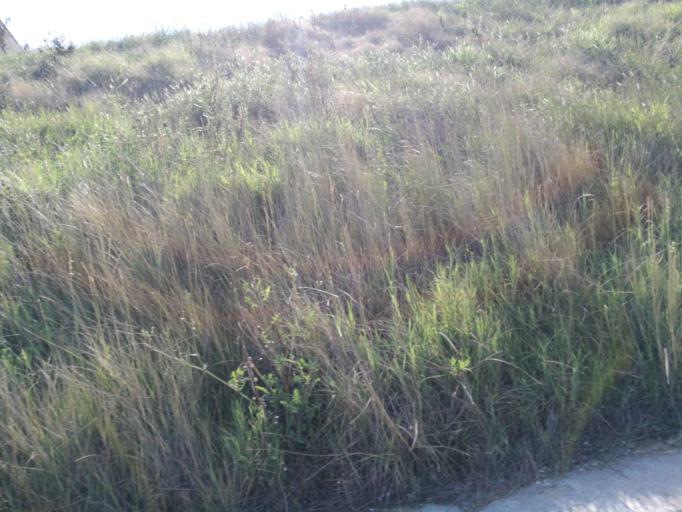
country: RO
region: Constanta
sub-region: Oras Eforie
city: Eforie
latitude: 44.0418
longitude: 28.6482
